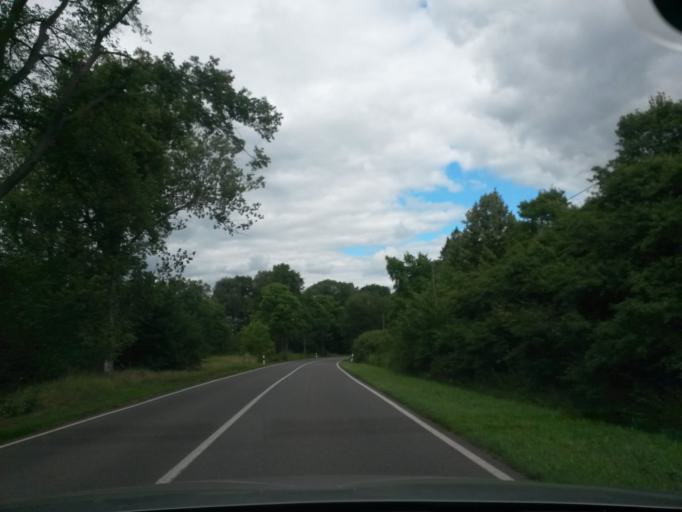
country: DE
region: Brandenburg
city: Angermunde
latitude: 52.9571
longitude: 13.9527
